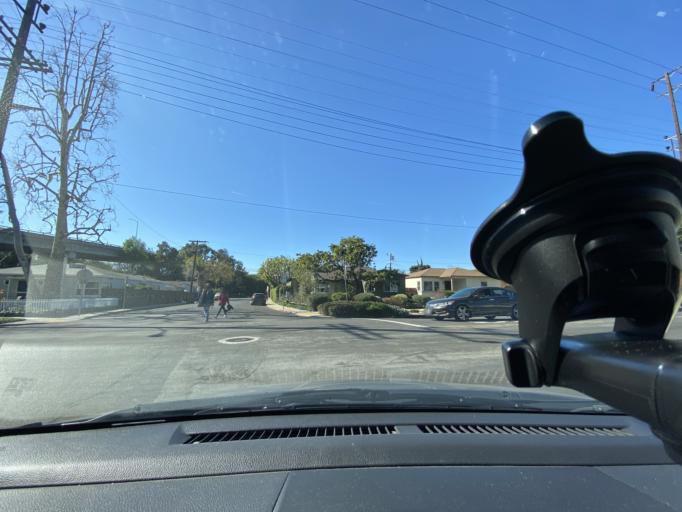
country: US
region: California
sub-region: Los Angeles County
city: Westwood, Los Angeles
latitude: 34.0328
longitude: -118.4287
